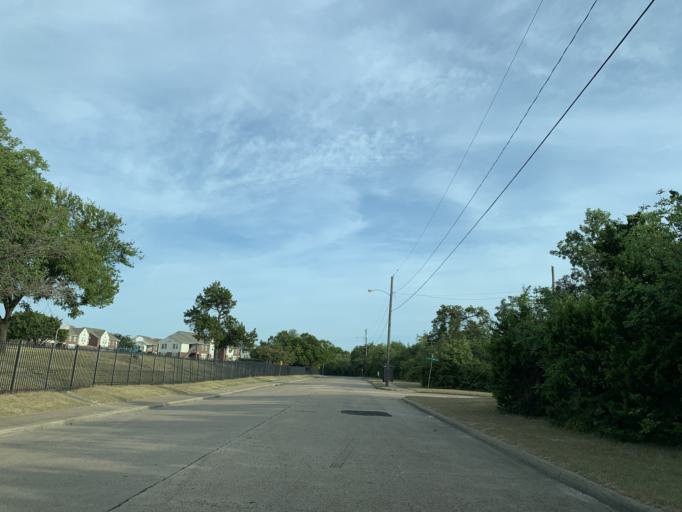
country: US
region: Texas
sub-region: Dallas County
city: Cockrell Hill
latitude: 32.6952
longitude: -96.9014
